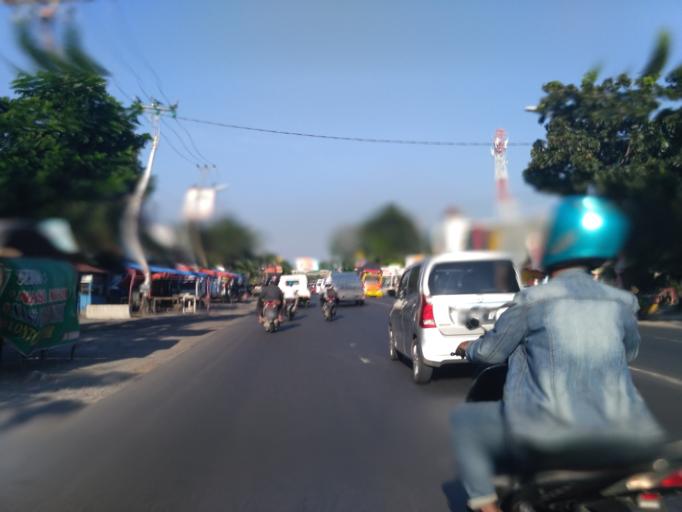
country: ID
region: Central Java
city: Semarang
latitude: -7.0070
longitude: 110.4589
